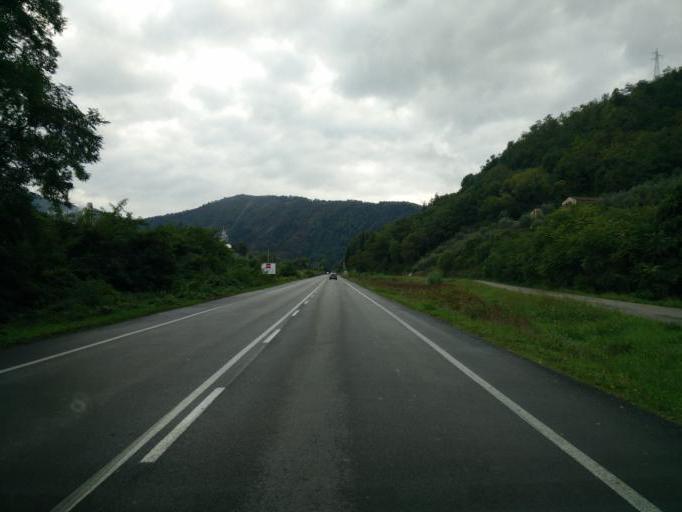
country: IT
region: Tuscany
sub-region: Provincia di Lucca
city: Valdottavo
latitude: 43.9514
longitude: 10.4999
